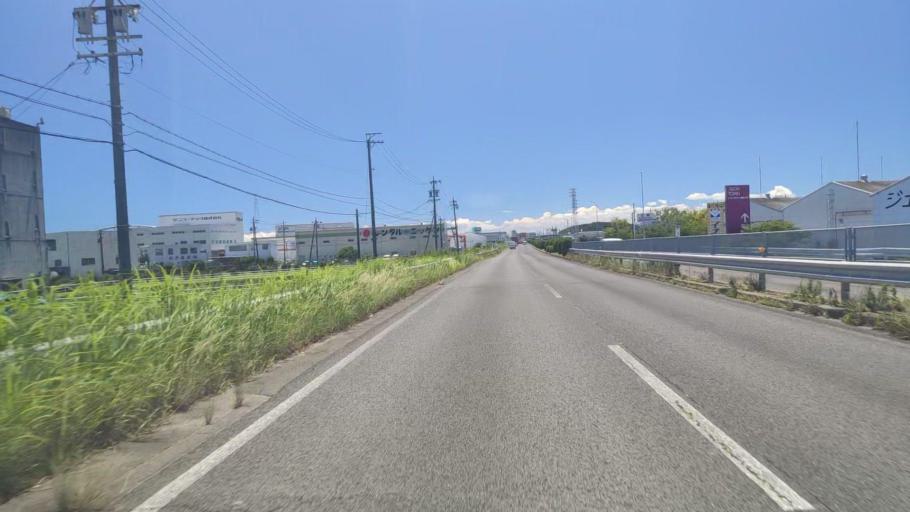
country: JP
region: Mie
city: Yokkaichi
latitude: 34.9208
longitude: 136.6125
